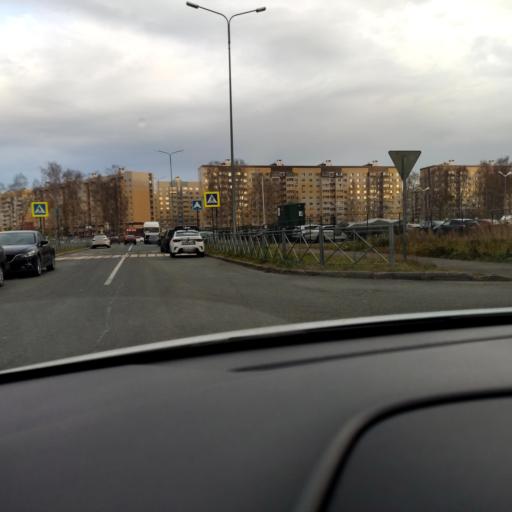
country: RU
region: Tatarstan
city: Osinovo
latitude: 55.8671
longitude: 48.8814
